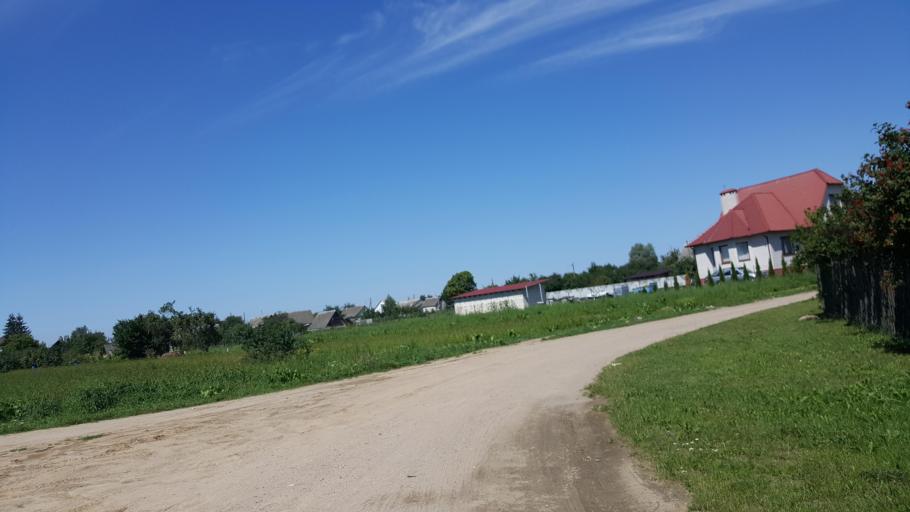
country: BY
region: Brest
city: Charnawchytsy
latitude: 52.2242
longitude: 23.7417
